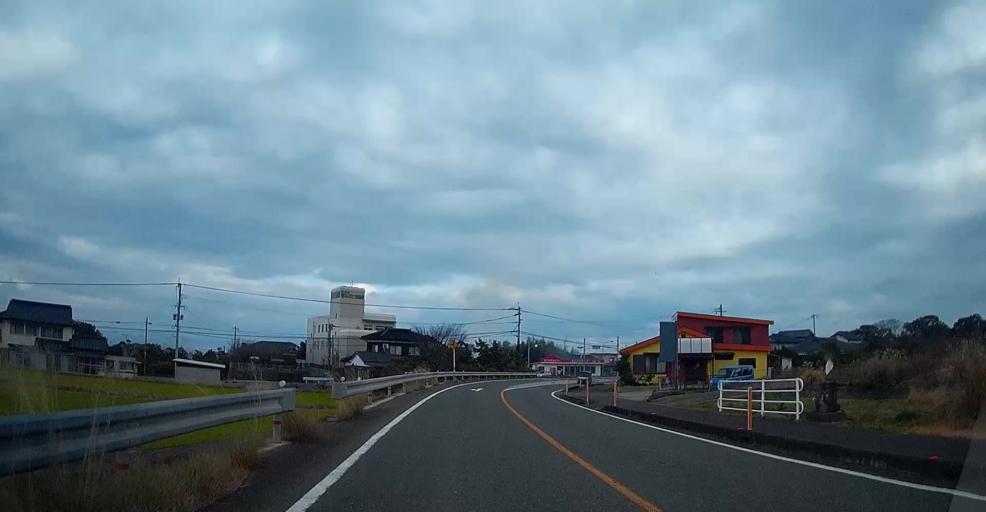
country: JP
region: Kumamoto
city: Hondo
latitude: 32.4764
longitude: 130.2607
